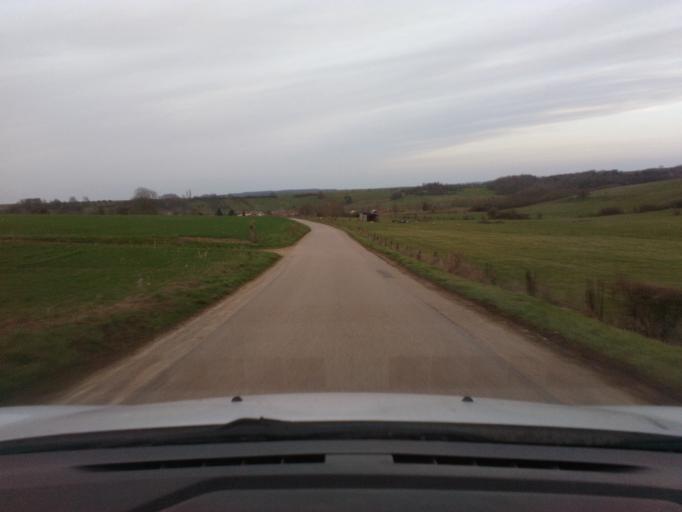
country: FR
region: Lorraine
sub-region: Departement des Vosges
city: Mirecourt
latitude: 48.3030
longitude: 6.0966
